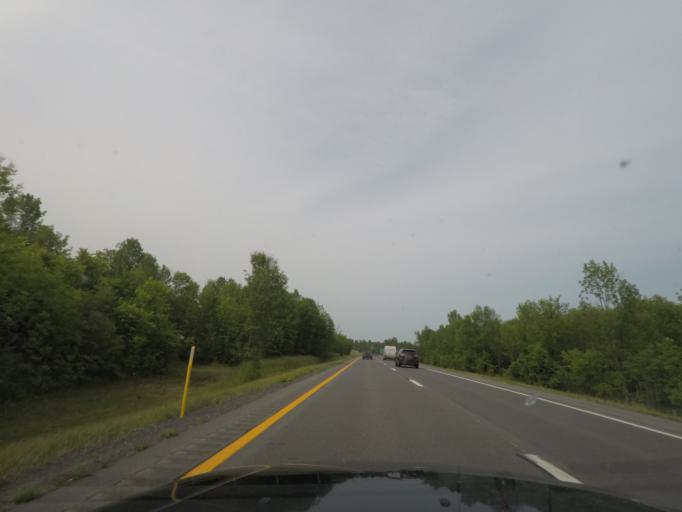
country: US
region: New York
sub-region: Clinton County
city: Peru
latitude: 44.6210
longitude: -73.4837
